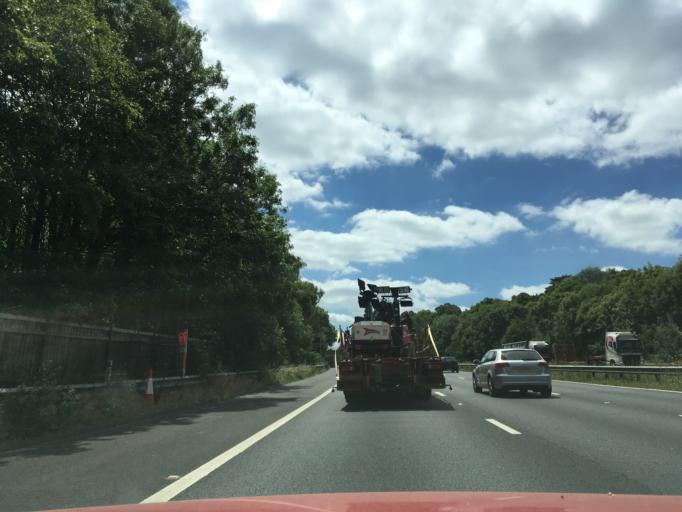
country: GB
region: England
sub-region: Hampshire
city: Compton
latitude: 51.0031
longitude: -1.3553
